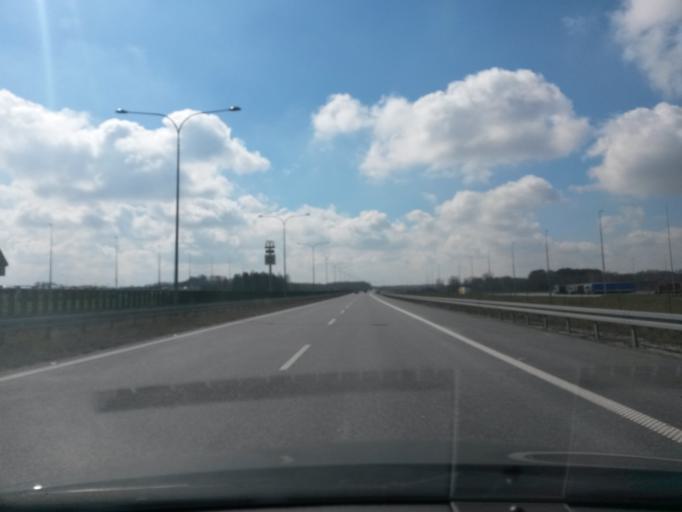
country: PL
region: Lodz Voivodeship
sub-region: powiat Lowicki
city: Bobrowniki
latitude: 52.0291
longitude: 20.0052
